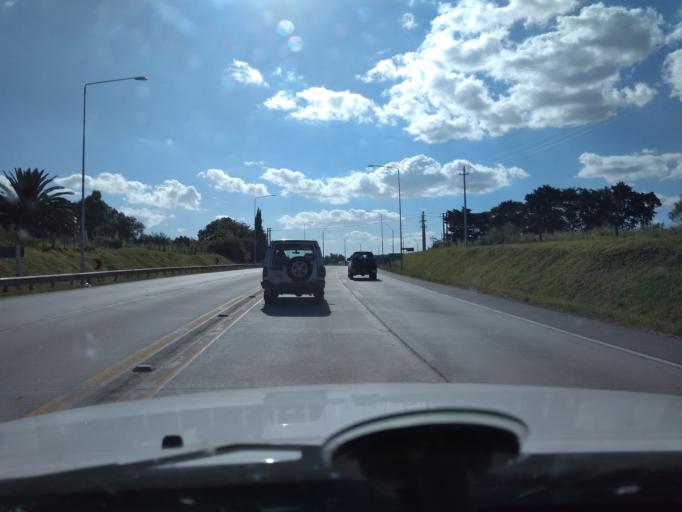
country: UY
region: Canelones
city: La Paz
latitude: -34.7832
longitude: -56.2485
